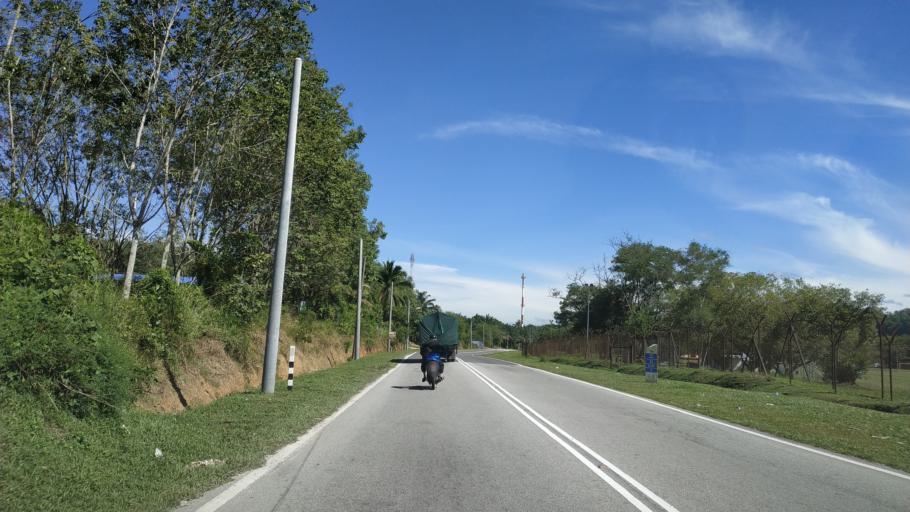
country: MY
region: Kedah
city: Kulim
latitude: 5.3309
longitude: 100.5344
